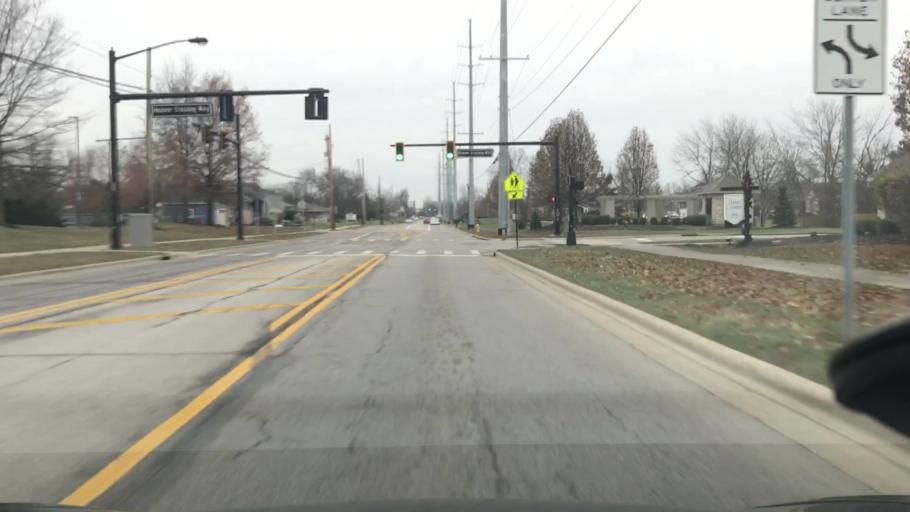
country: US
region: Ohio
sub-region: Franklin County
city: Grove City
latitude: 39.8661
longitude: -83.0708
